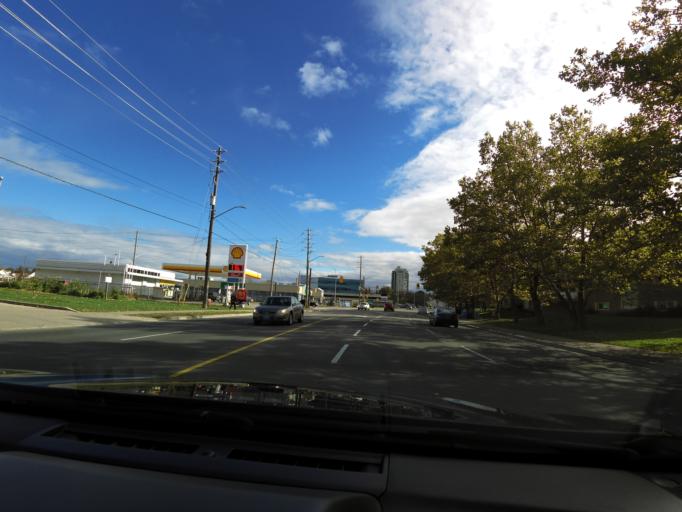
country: CA
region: Ontario
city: Waterloo
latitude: 43.4633
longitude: -80.5397
